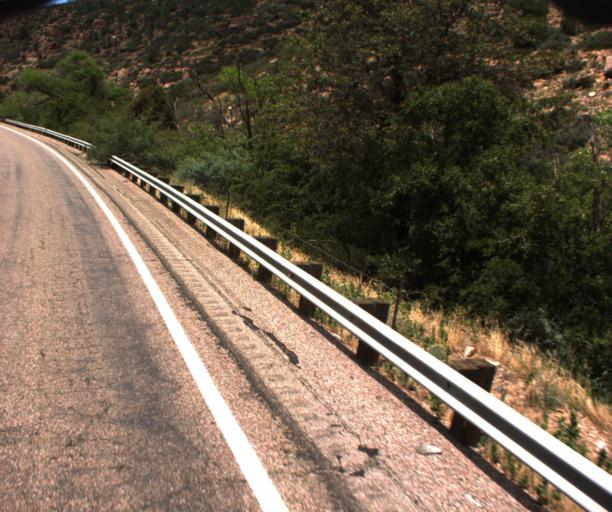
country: US
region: Arizona
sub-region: Pinal County
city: Superior
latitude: 33.3396
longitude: -111.0188
